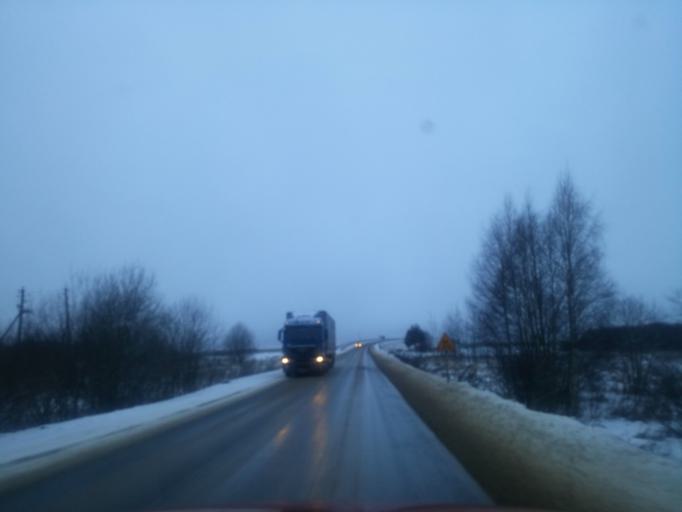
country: RU
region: Tverskaya
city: Likhoslavl'
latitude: 56.9725
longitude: 35.4332
